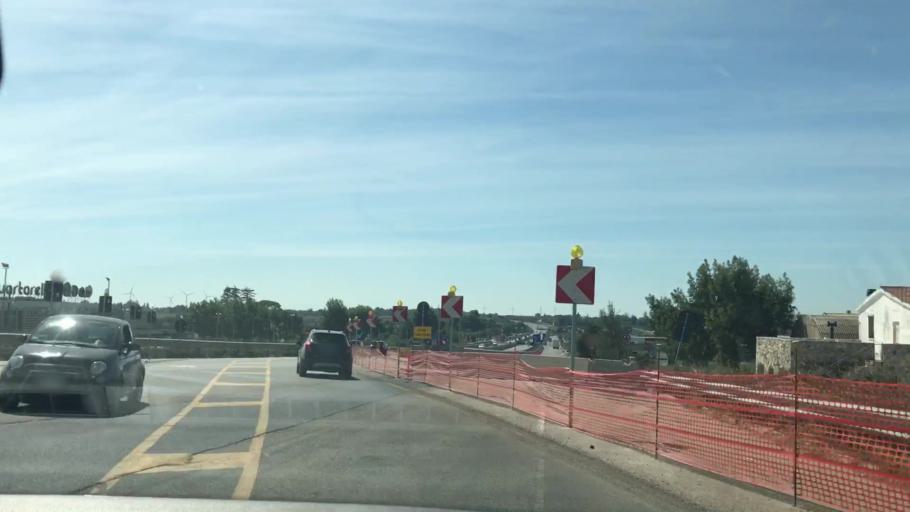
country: IT
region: Apulia
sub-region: Provincia di Bari
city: Altamura
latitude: 40.8068
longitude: 16.5555
